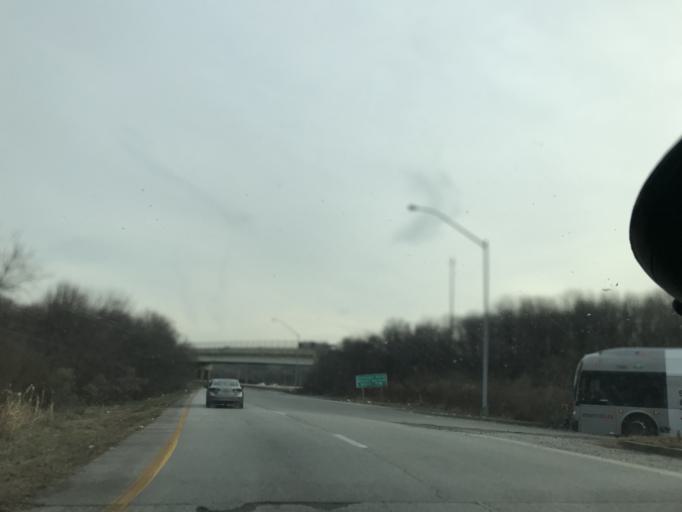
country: US
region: Maryland
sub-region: Prince George's County
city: Glenarden
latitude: 38.9436
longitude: -76.8724
